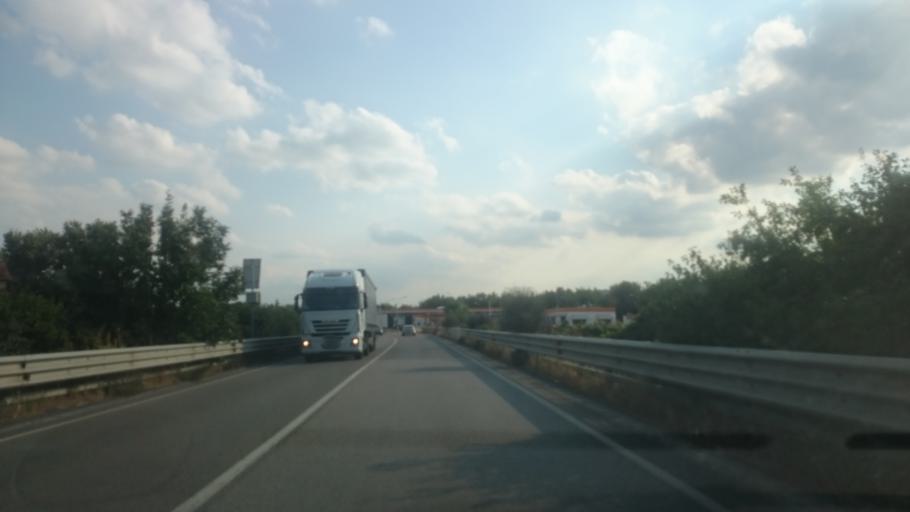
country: IT
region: Emilia-Romagna
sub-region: Provincia di Reggio Emilia
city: Salvaterra
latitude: 44.5967
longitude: 10.7762
